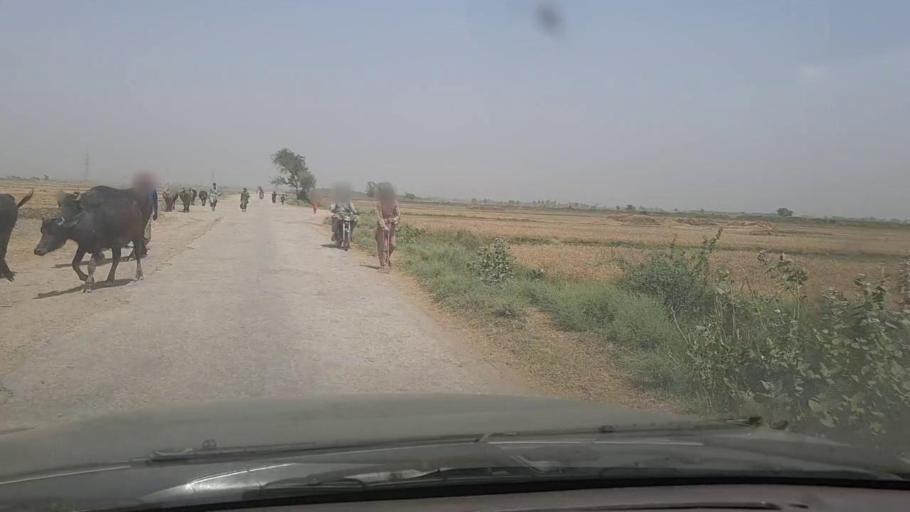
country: PK
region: Sindh
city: Madeji
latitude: 27.8055
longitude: 68.4002
